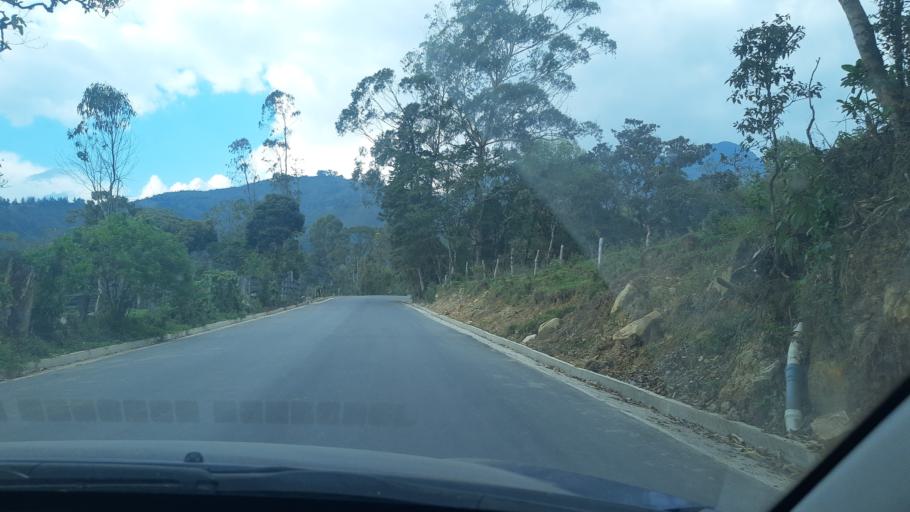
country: CO
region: Boyaca
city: Garagoa
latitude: 5.0887
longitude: -73.3464
